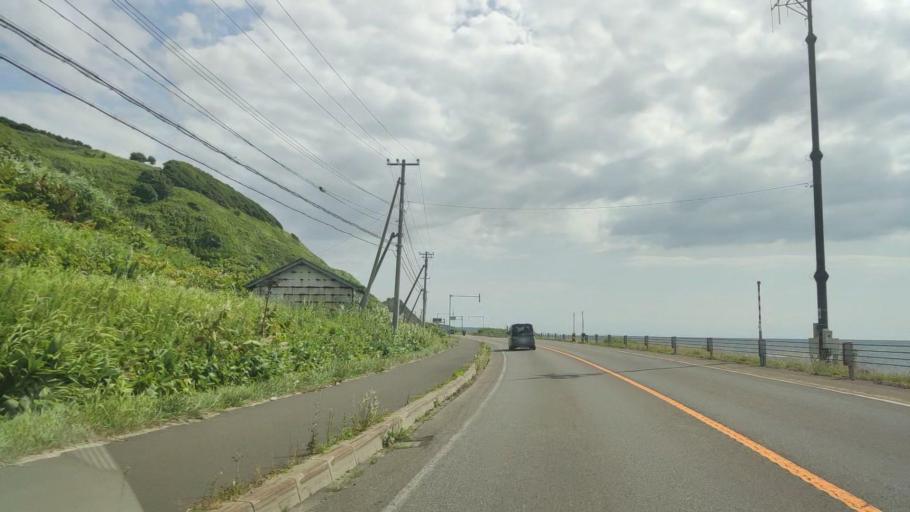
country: JP
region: Hokkaido
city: Rumoi
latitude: 44.2223
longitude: 141.6551
